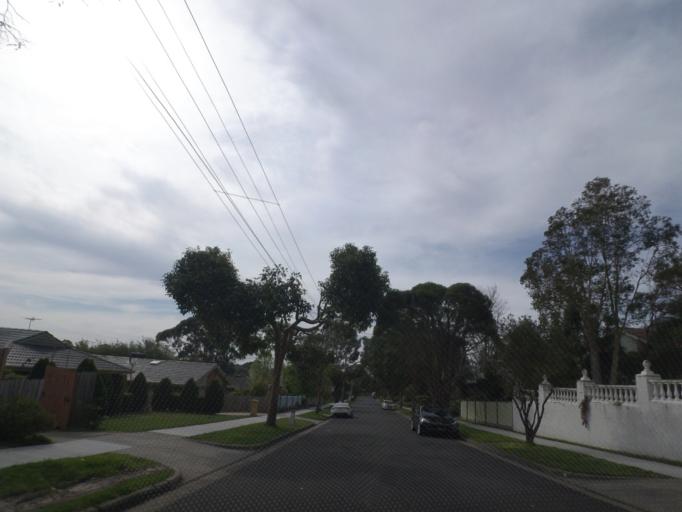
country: AU
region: Victoria
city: Mitcham
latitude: -37.8103
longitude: 145.2038
